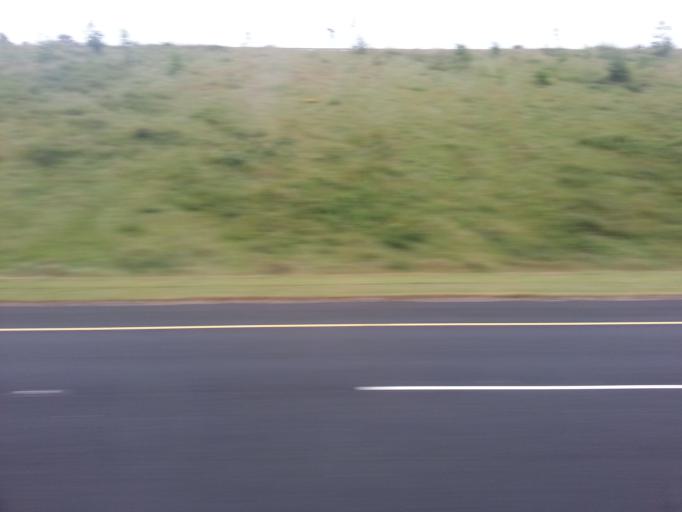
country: IE
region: Leinster
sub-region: Kildare
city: Moone
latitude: 53.0135
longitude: -6.8297
